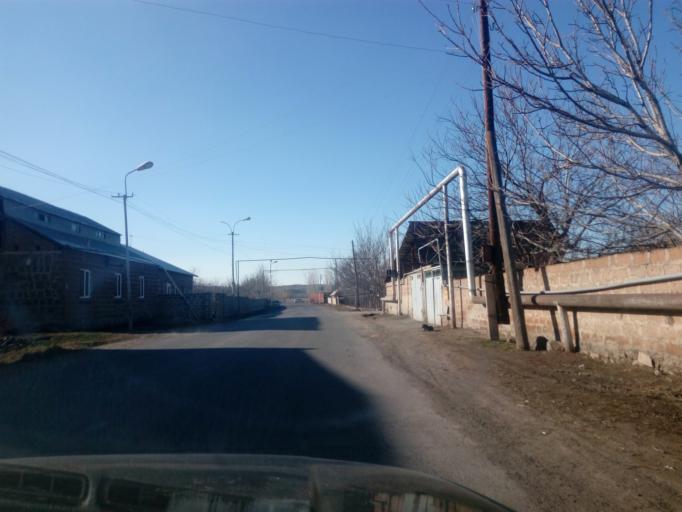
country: AM
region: Kotayk'i Marz
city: Akunk'
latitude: 40.2684
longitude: 44.6833
